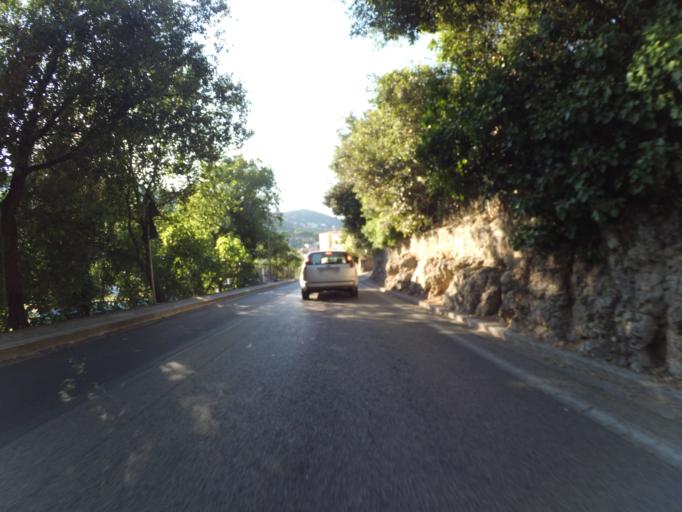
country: IT
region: Latium
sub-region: Provincia di Latina
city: San Felice Circeo
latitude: 41.2345
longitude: 13.0906
